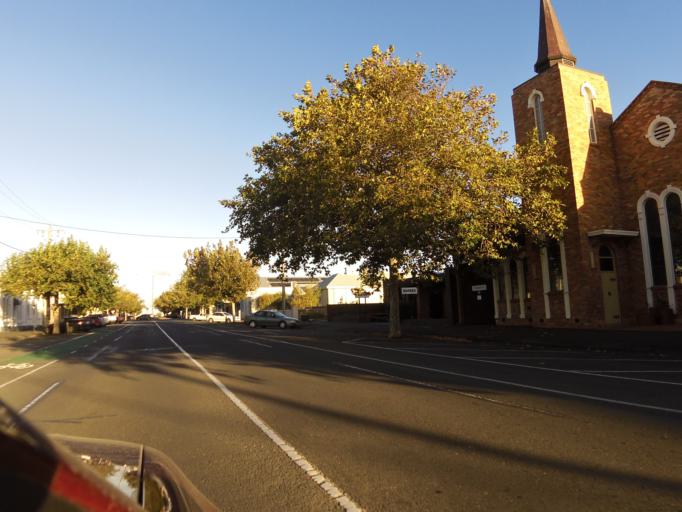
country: AU
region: Victoria
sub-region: Warrnambool
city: Warrnambool
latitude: -38.3820
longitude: 142.4799
